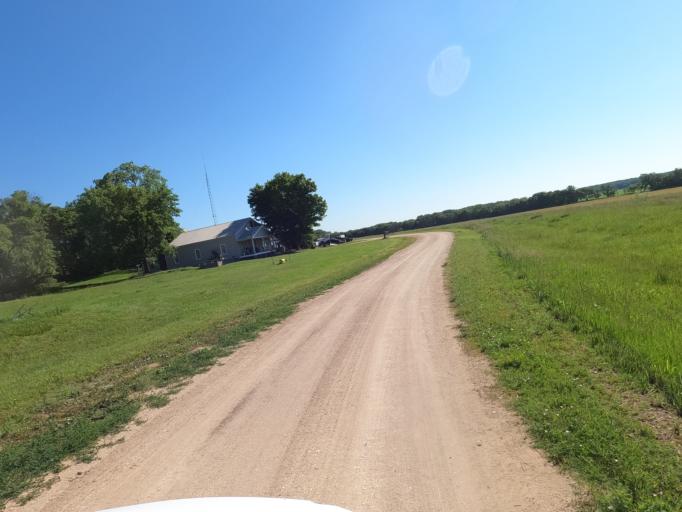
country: US
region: Kansas
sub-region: Marion County
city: Marion
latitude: 38.2635
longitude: -96.8514
